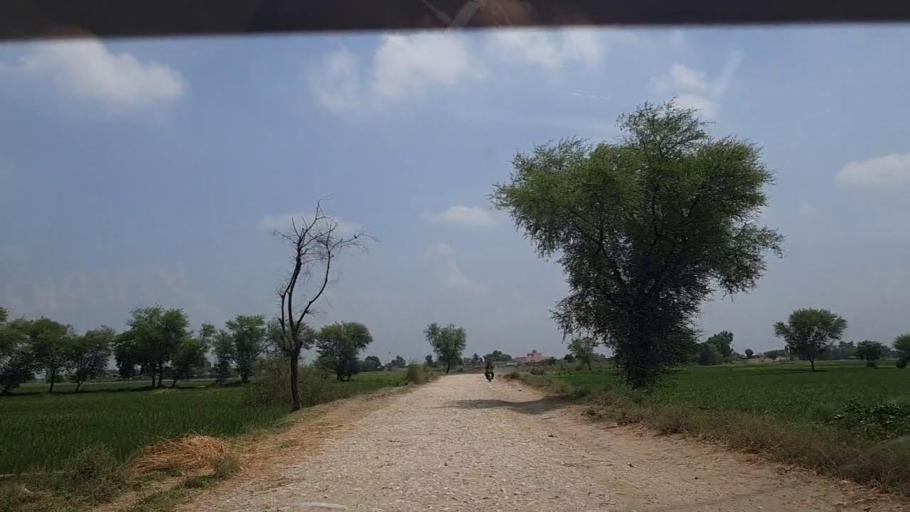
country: PK
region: Sindh
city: Khanpur
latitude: 27.8901
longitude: 69.4040
